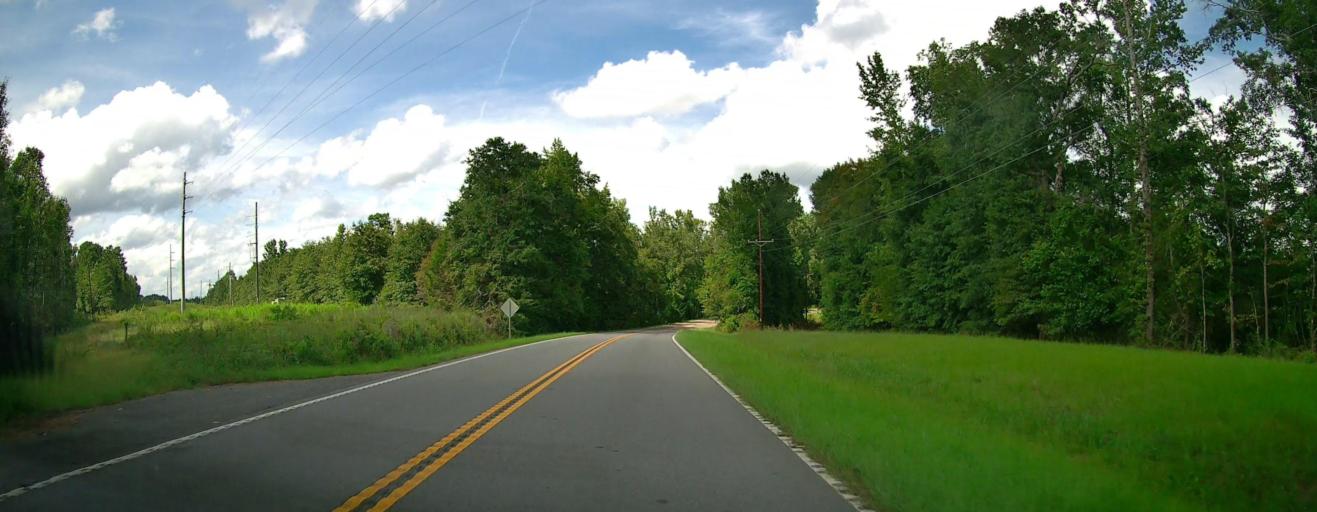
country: US
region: Georgia
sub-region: Talbot County
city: Talbotton
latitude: 32.6201
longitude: -84.4884
